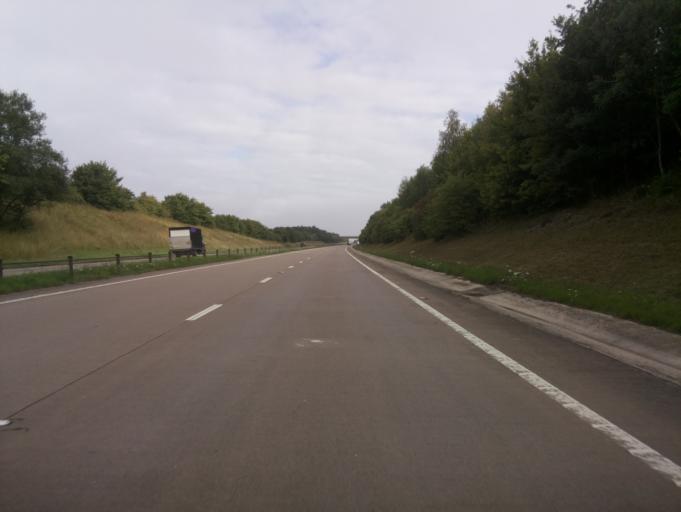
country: GB
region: England
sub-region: Gloucestershire
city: Cirencester
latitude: 51.6916
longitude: -1.9132
